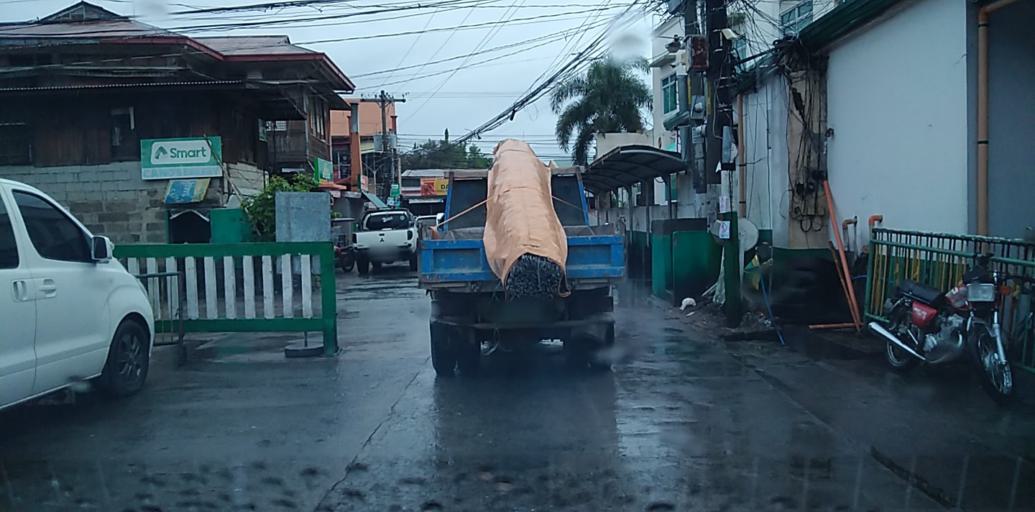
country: PH
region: Central Luzon
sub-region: Province of Pampanga
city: Mexico
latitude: 15.0654
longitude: 120.7198
